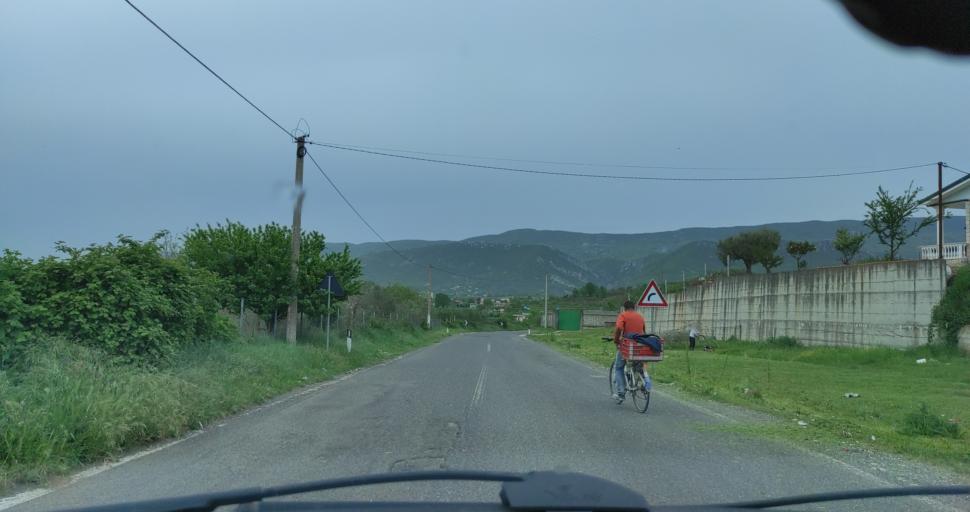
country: AL
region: Lezhe
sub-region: Rrethi i Kurbinit
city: Mamurras
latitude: 41.5879
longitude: 19.6933
